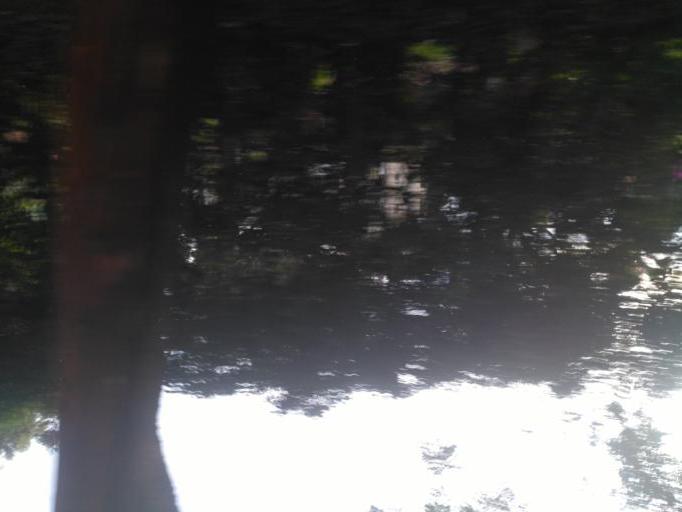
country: UG
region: Eastern Region
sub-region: Jinja District
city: Jinja
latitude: 0.4362
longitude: 33.2005
